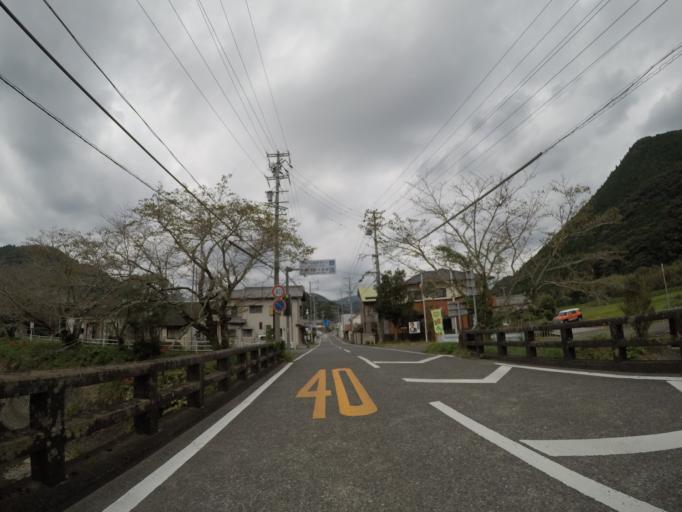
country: JP
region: Shizuoka
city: Fujieda
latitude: 34.9018
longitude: 138.1993
